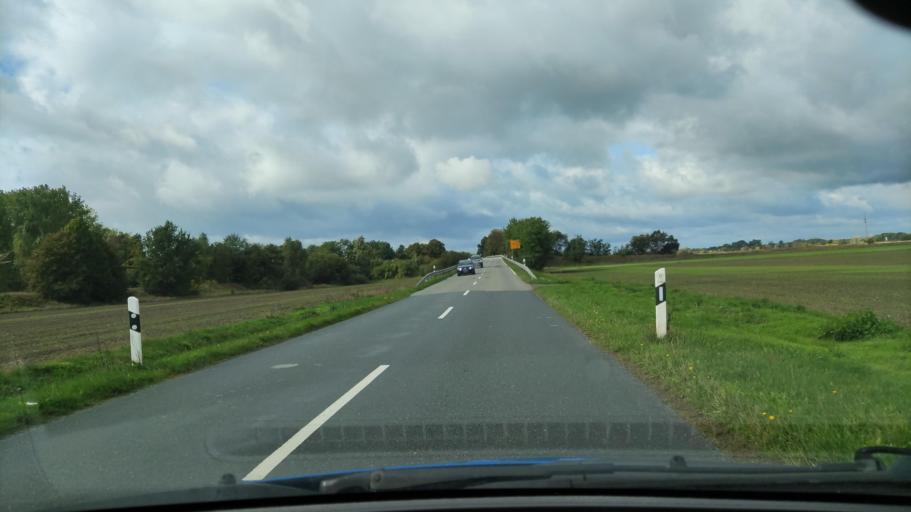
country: DE
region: Saxony-Anhalt
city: Salzwedel
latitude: 52.8545
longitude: 11.1905
